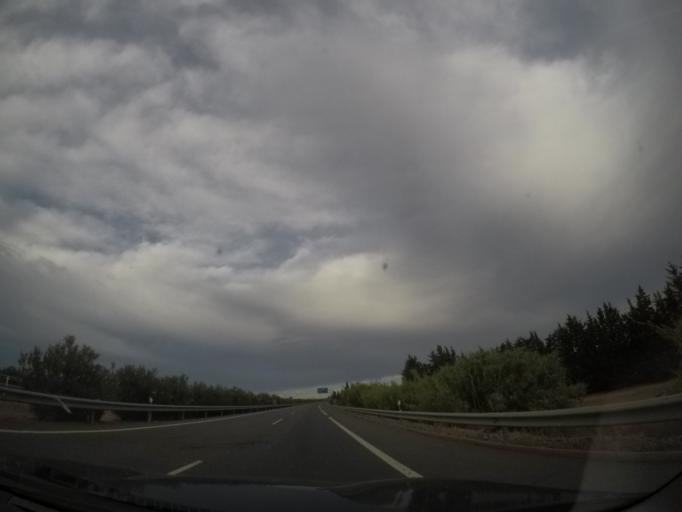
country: ES
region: Andalusia
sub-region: Provincia de Huelva
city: Aljaraque
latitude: 37.3237
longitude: -7.0628
